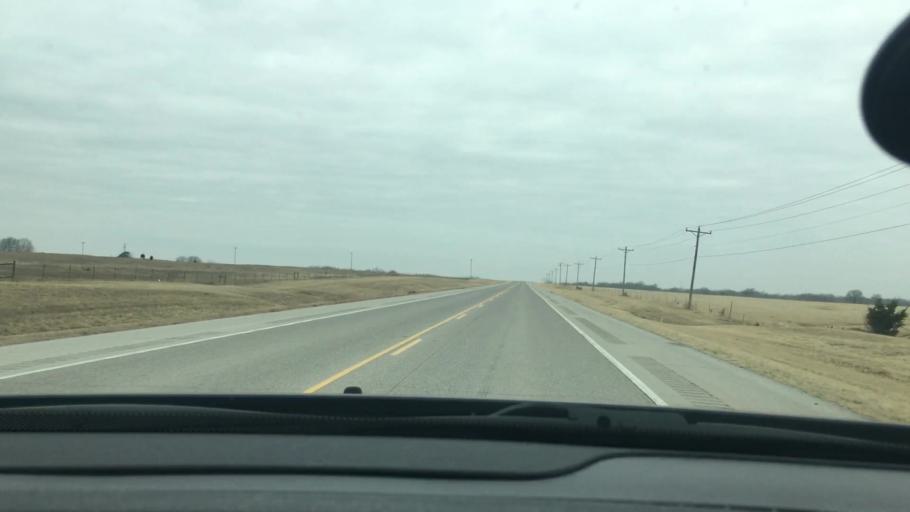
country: US
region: Oklahoma
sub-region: Murray County
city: Davis
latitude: 34.5213
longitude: -97.2921
